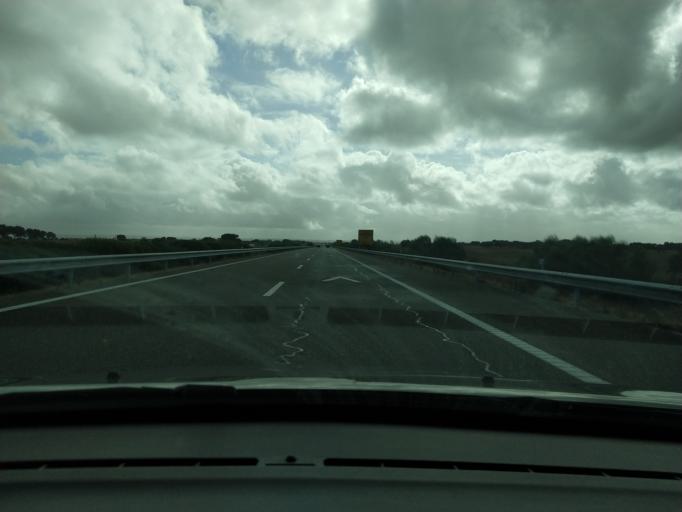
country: PT
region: Beja
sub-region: Ourique
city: Ourique
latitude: 37.5974
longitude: -8.1745
